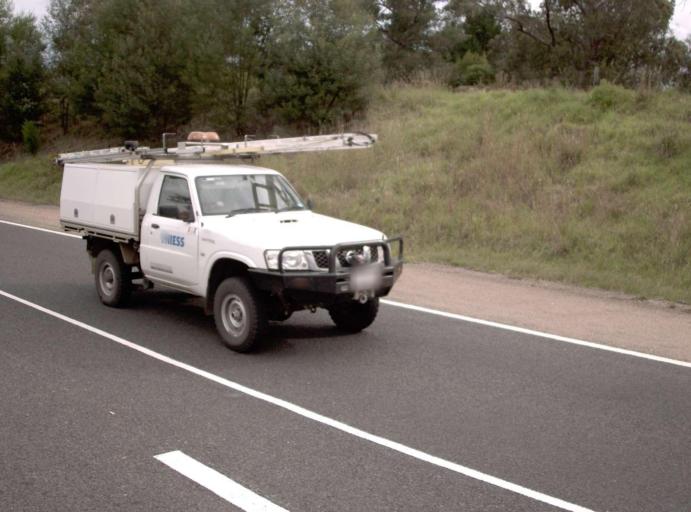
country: AU
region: Victoria
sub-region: East Gippsland
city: Lakes Entrance
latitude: -37.7304
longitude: 148.0897
